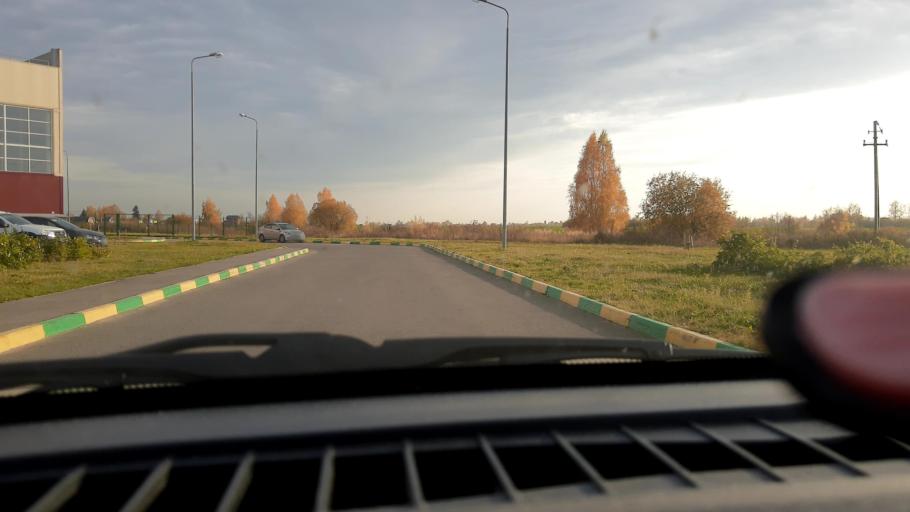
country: RU
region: Nizjnij Novgorod
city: Gorodets
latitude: 56.6390
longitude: 43.4908
